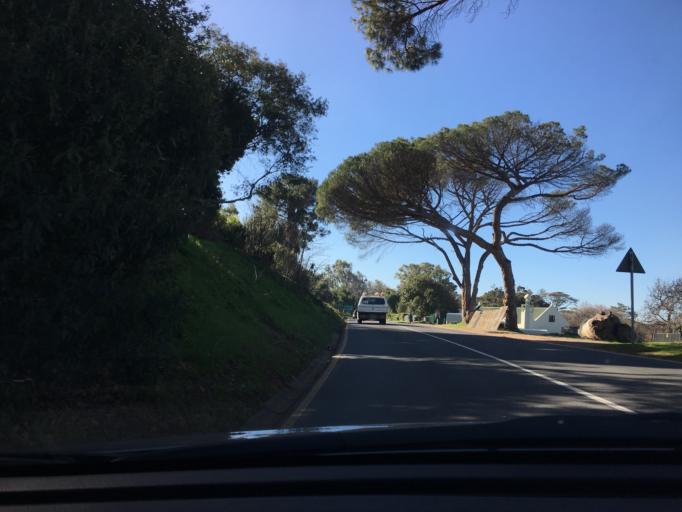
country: ZA
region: Western Cape
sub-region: City of Cape Town
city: Constantia
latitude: -34.0239
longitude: 18.4359
